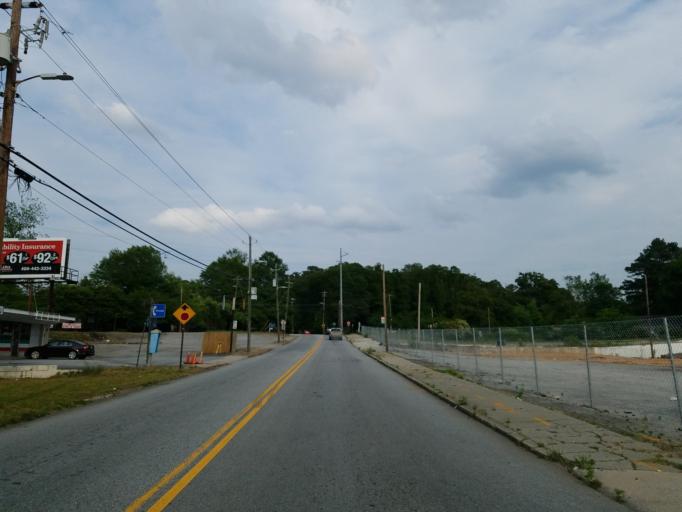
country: US
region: Georgia
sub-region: Cobb County
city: Vinings
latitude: 33.8205
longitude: -84.4505
